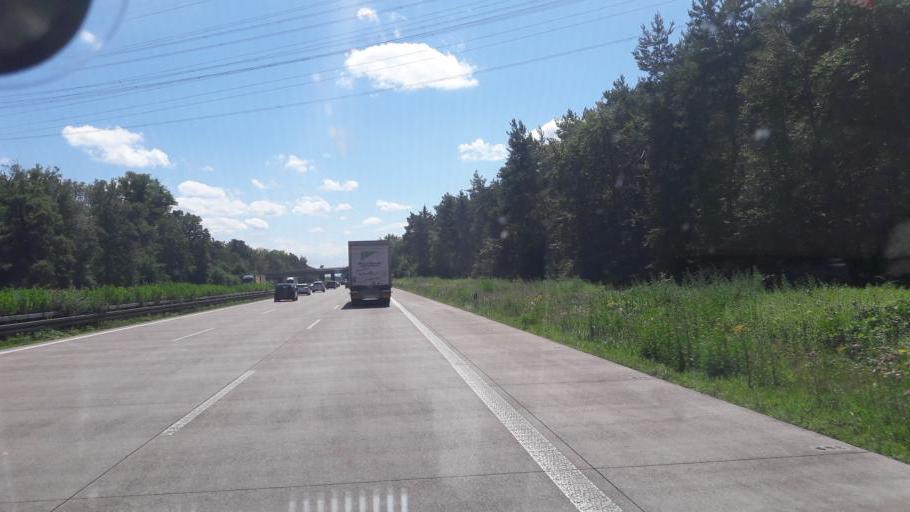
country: DE
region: Baden-Wuerttemberg
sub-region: Karlsruhe Region
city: Forst
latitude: 49.1822
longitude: 8.5801
